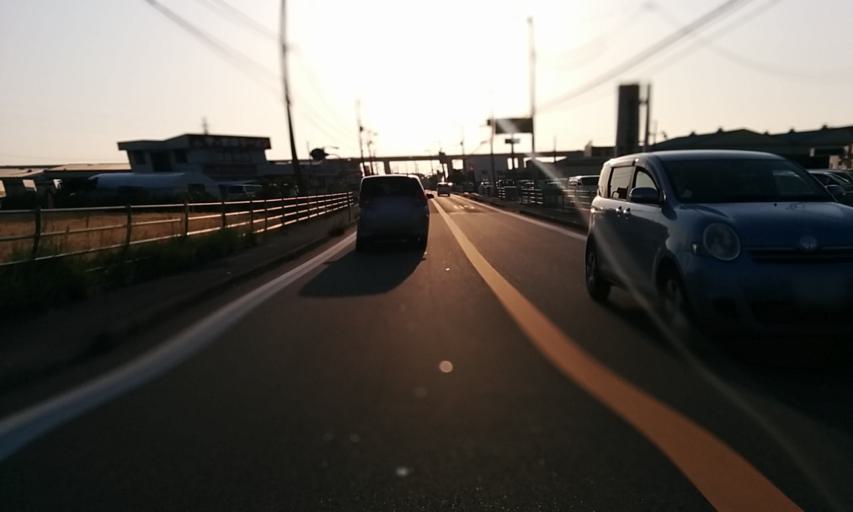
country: JP
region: Ehime
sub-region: Shikoku-chuo Shi
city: Matsuyama
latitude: 33.7894
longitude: 132.7764
